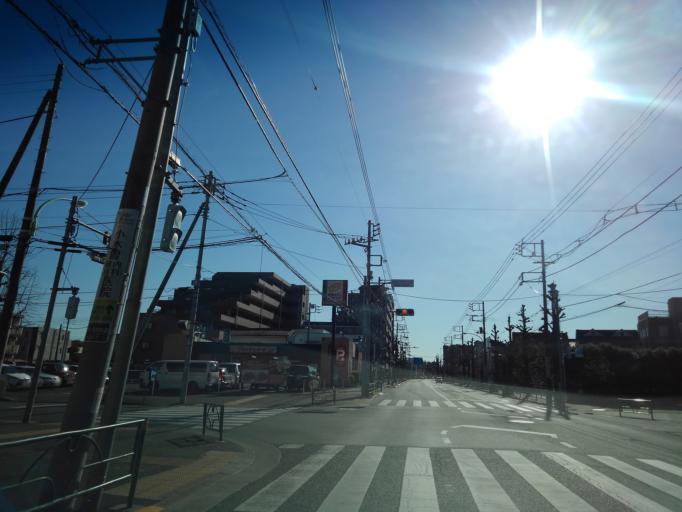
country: JP
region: Tokyo
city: Kokubunji
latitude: 35.6777
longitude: 139.4990
